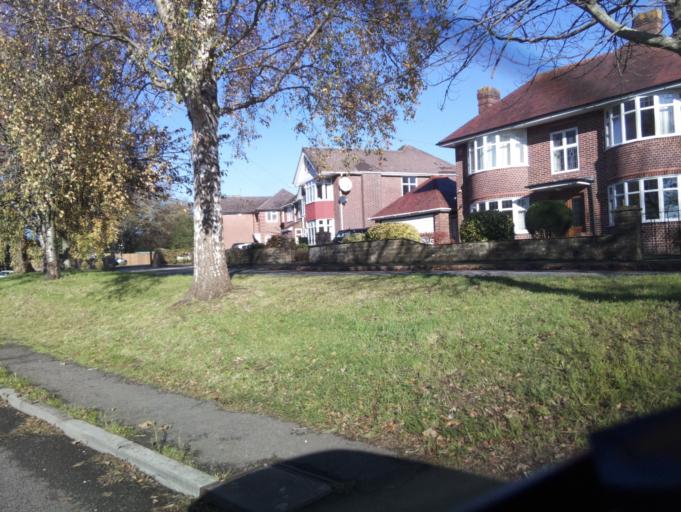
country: GB
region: England
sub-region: Somerset
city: Yeovil
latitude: 50.9542
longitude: -2.6479
